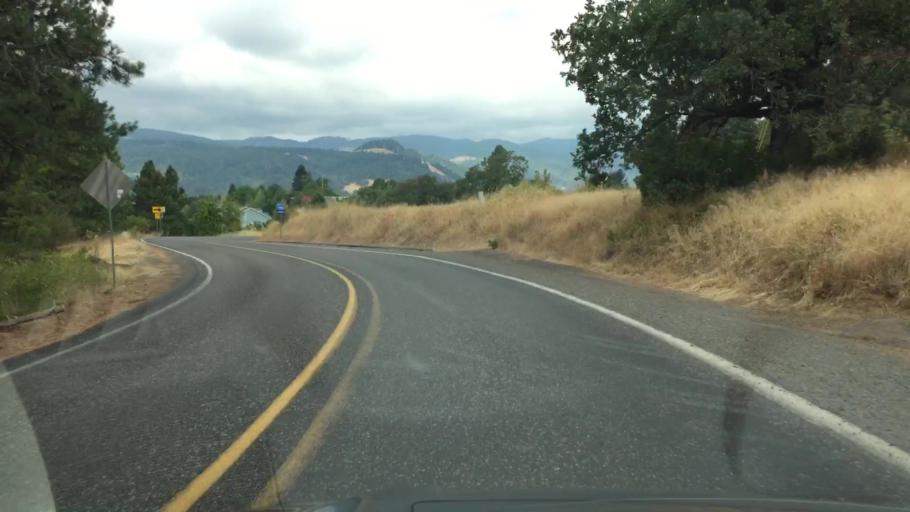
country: US
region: Washington
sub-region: Klickitat County
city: White Salmon
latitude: 45.7329
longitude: -121.5073
